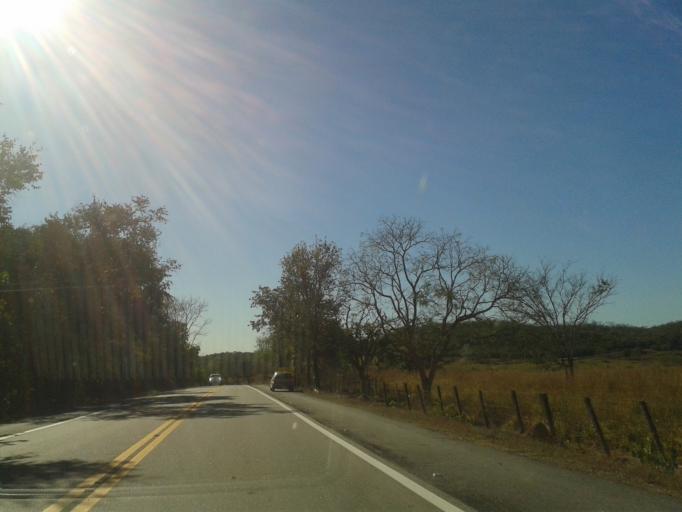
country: BR
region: Goias
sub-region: Itapuranga
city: Itapuranga
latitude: -15.3941
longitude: -50.3857
